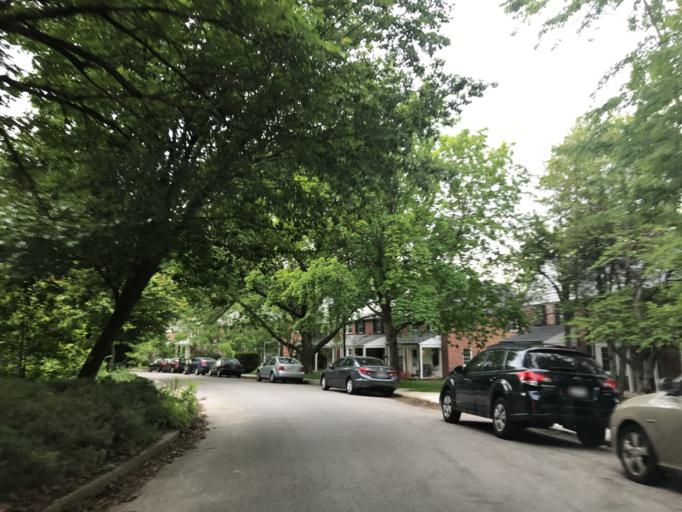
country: US
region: Maryland
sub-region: City of Baltimore
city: Baltimore
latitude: 39.3425
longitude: -76.5964
